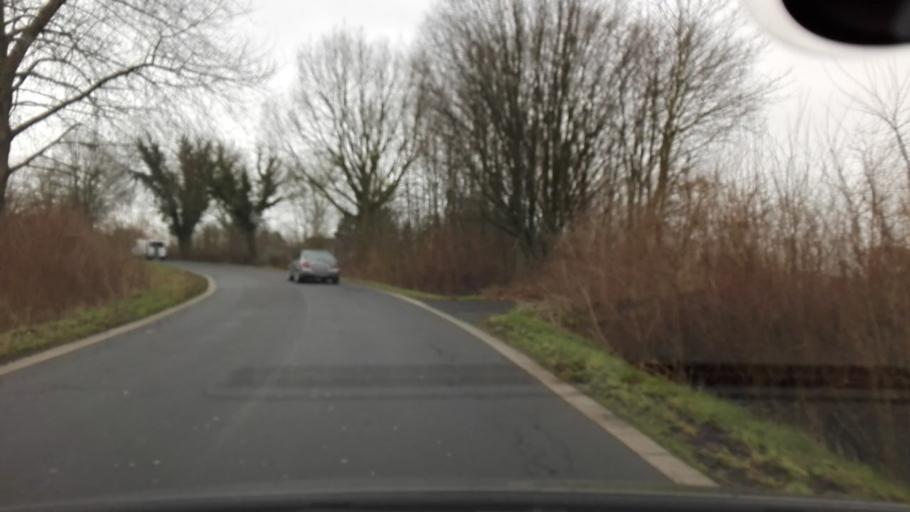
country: DE
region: North Rhine-Westphalia
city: Kamen
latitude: 51.5785
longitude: 7.6440
